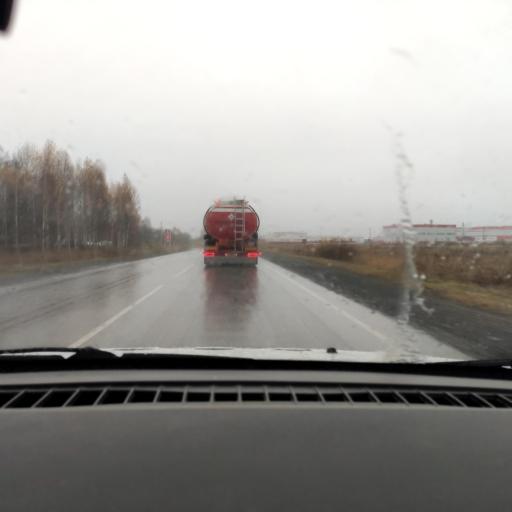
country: RU
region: Perm
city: Froly
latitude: 57.8984
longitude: 56.2372
